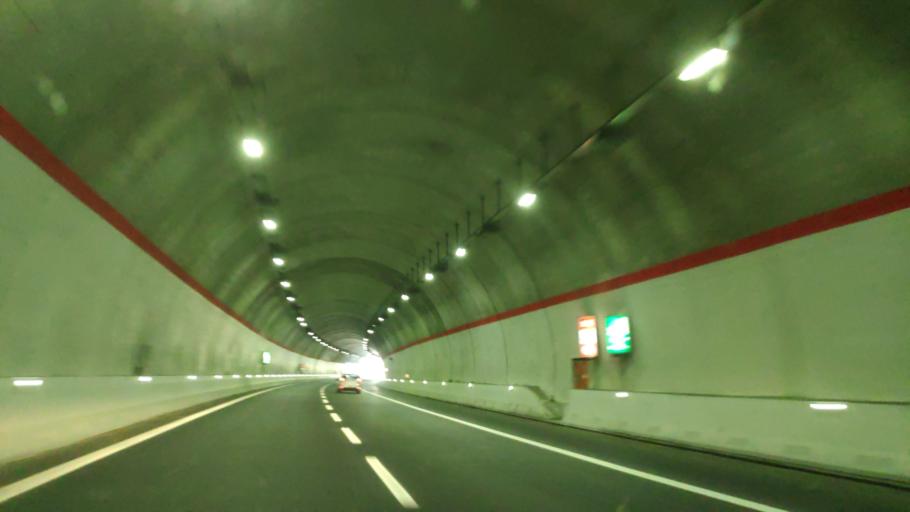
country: IT
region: Basilicate
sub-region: Provincia di Potenza
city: Lagonegro
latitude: 40.1126
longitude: 15.7887
